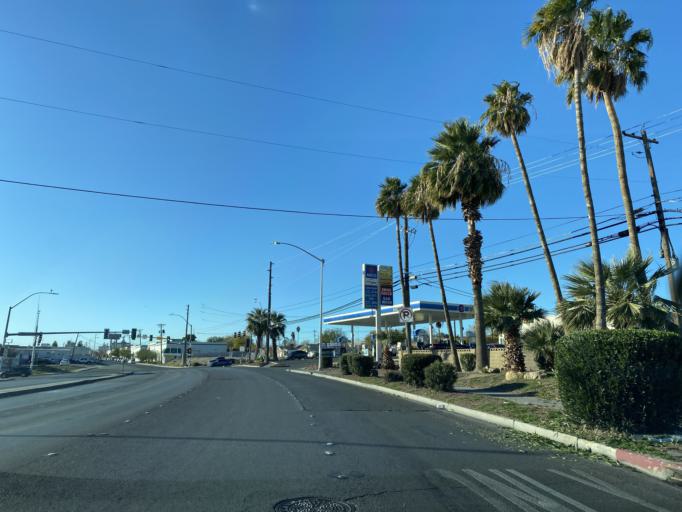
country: US
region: Nevada
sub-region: Clark County
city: Las Vegas
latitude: 36.1967
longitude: -115.1427
